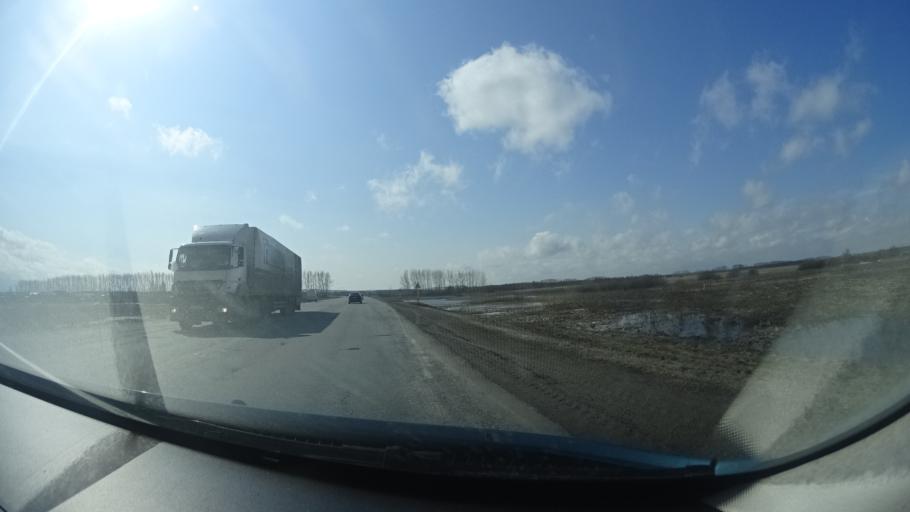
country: RU
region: Bashkortostan
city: Mikhaylovka
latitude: 54.9270
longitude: 55.7393
